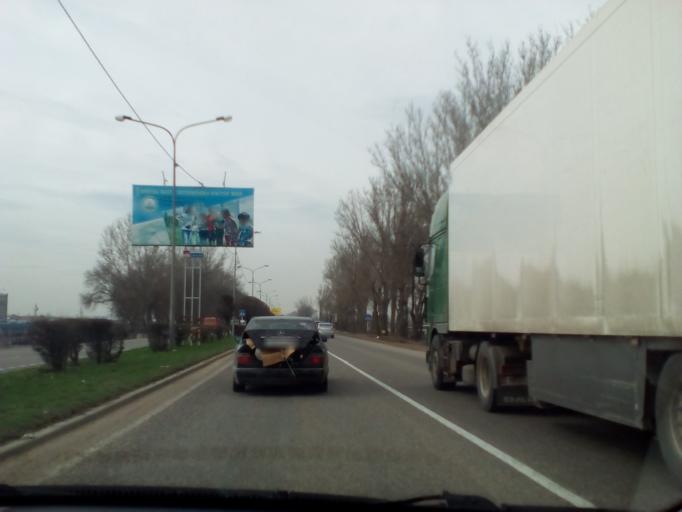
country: KZ
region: Almaty Oblysy
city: Burunday
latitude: 43.2197
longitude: 76.6374
